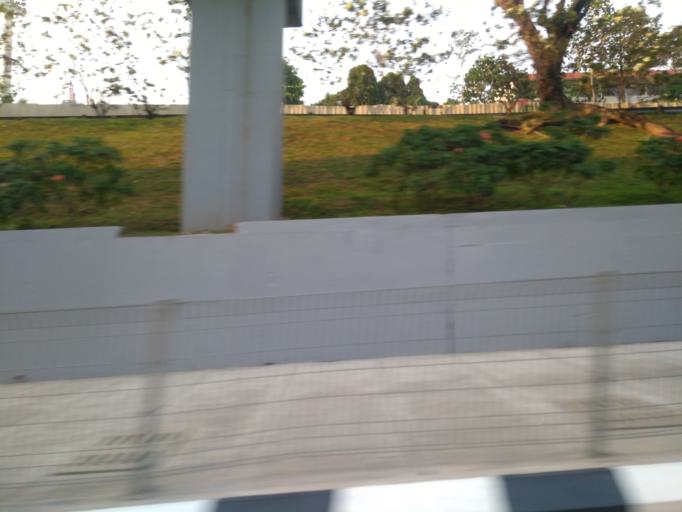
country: MY
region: Kuala Lumpur
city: Kuala Lumpur
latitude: 3.1375
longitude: 101.7011
